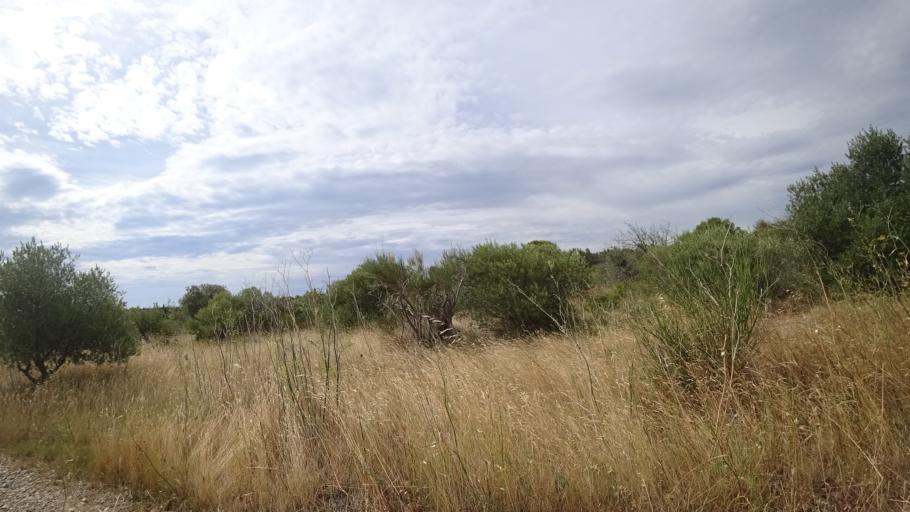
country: FR
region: Languedoc-Roussillon
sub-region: Departement de l'Aude
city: Leucate
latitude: 42.9067
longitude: 3.0256
